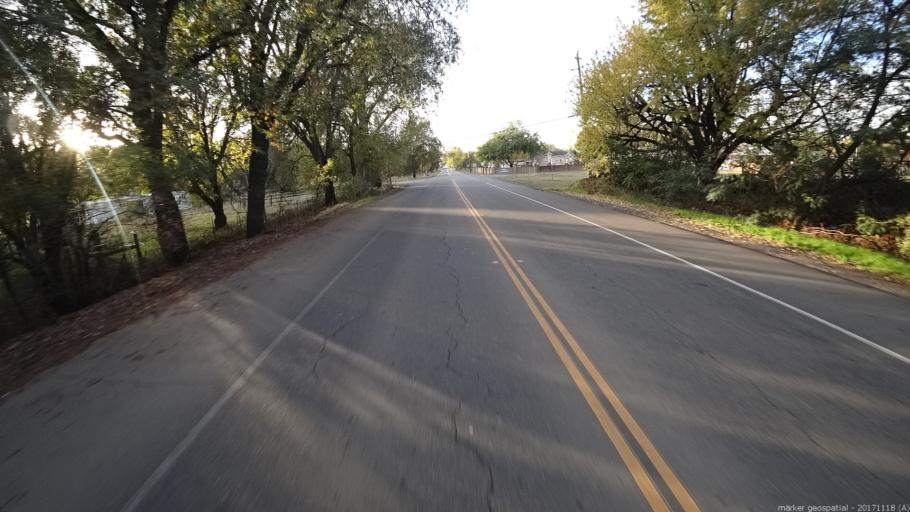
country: US
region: California
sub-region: Shasta County
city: Anderson
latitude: 40.4677
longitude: -122.3112
